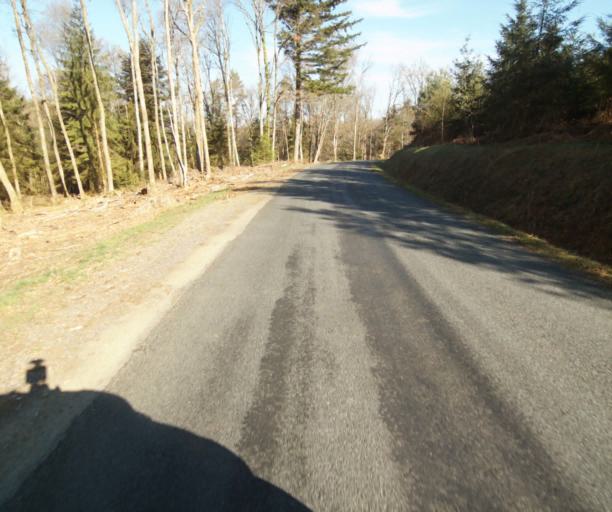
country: FR
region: Limousin
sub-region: Departement de la Correze
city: Correze
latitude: 45.2907
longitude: 1.8694
